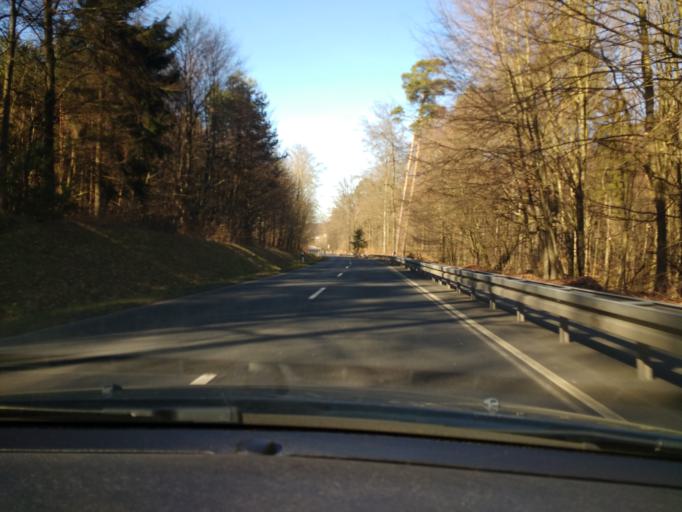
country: DE
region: Bavaria
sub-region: Regierungsbezirk Unterfranken
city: Alzenau in Unterfranken
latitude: 50.1307
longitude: 9.0721
